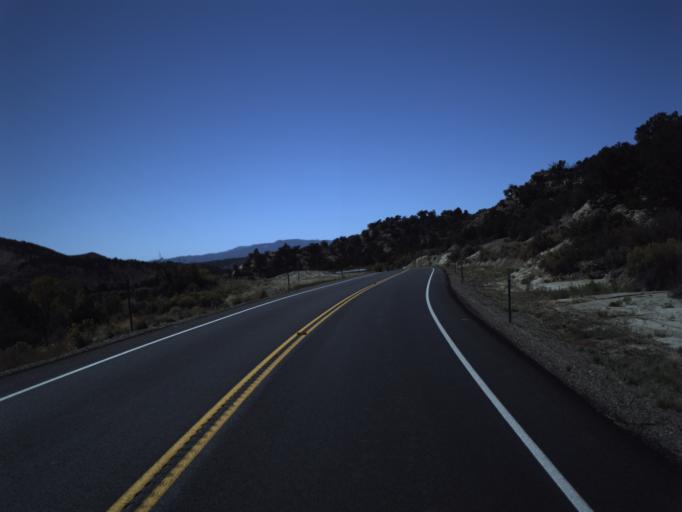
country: US
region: Utah
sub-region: Garfield County
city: Panguitch
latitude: 37.5947
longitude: -111.9235
